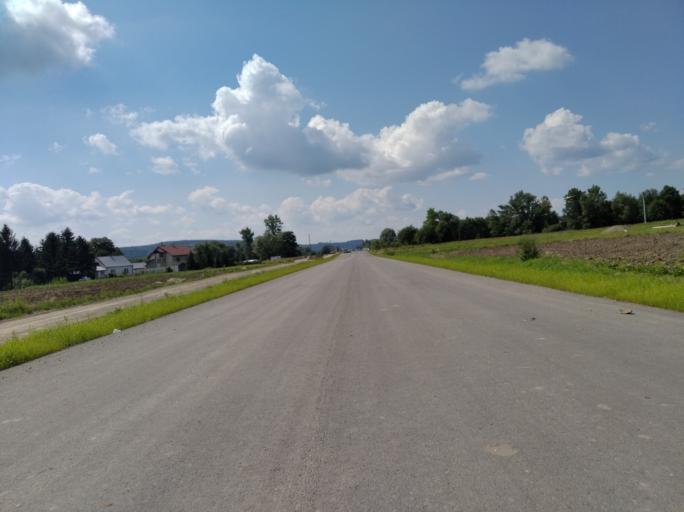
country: PL
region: Subcarpathian Voivodeship
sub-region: Powiat rzeszowski
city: Dynow
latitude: 49.8293
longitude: 22.2416
